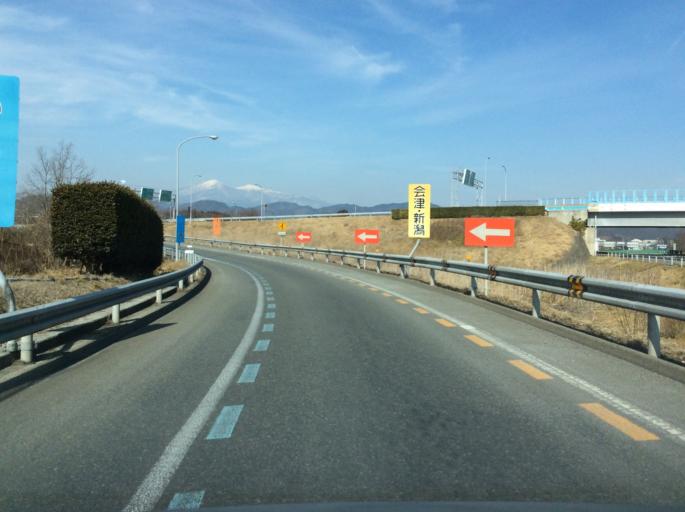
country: JP
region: Fukushima
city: Motomiya
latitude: 37.4643
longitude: 140.3605
